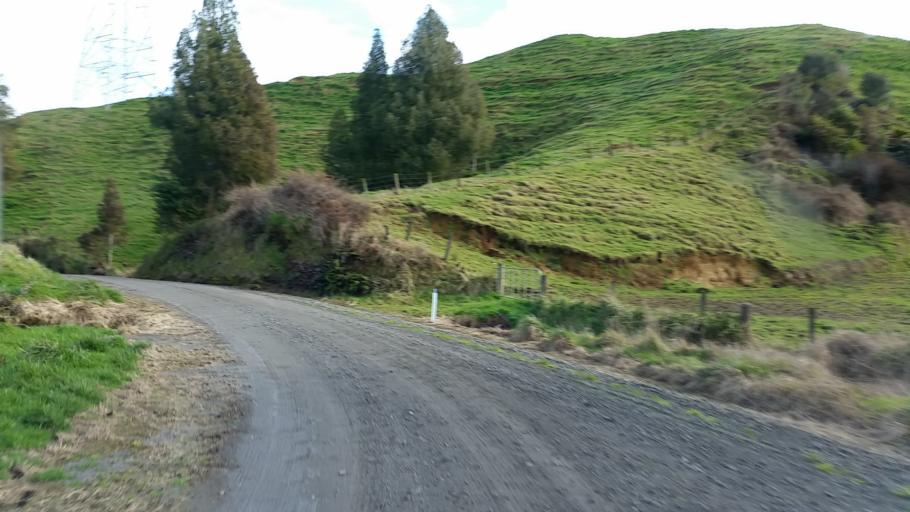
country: NZ
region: Taranaki
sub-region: South Taranaki District
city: Eltham
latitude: -39.2548
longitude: 174.5226
